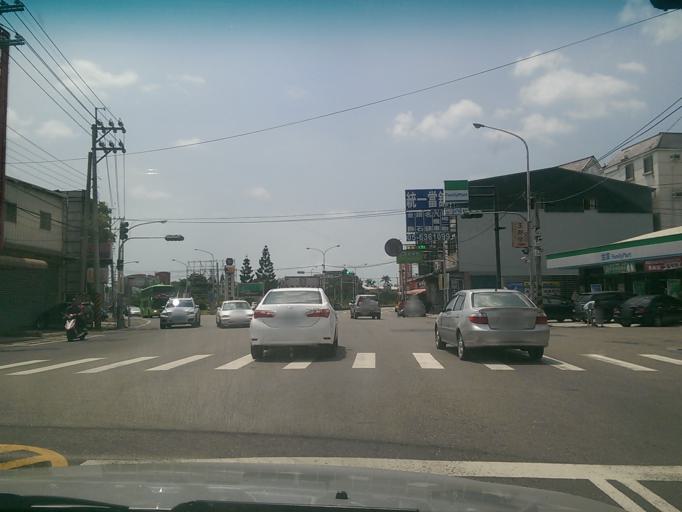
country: TW
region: Taiwan
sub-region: Yunlin
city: Douliu
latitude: 23.7092
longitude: 120.4466
